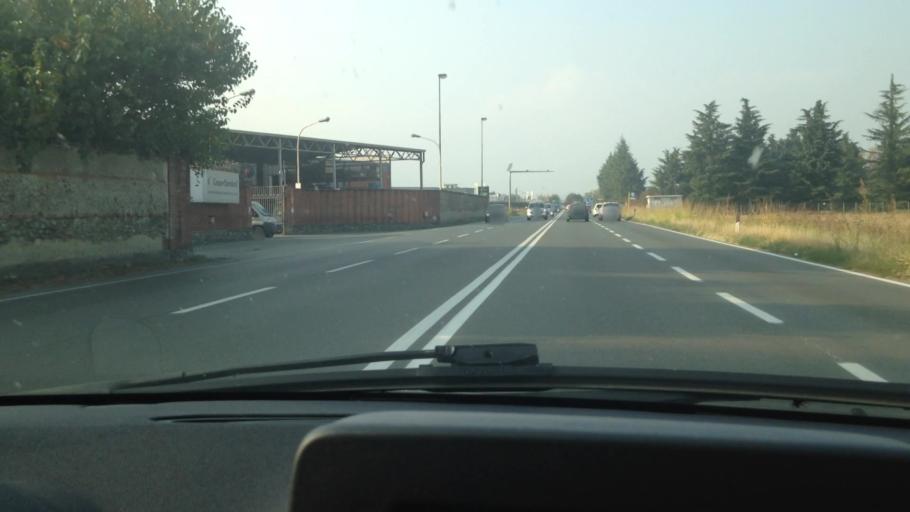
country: IT
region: Piedmont
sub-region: Provincia di Torino
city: San Maurizio
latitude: 45.2113
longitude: 7.6152
